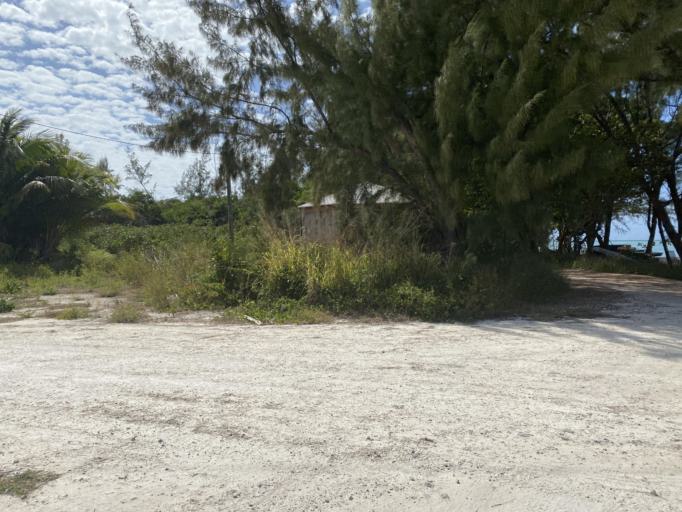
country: BS
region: Spanish Wells
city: Spanish Wells
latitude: 25.5472
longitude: -76.7715
